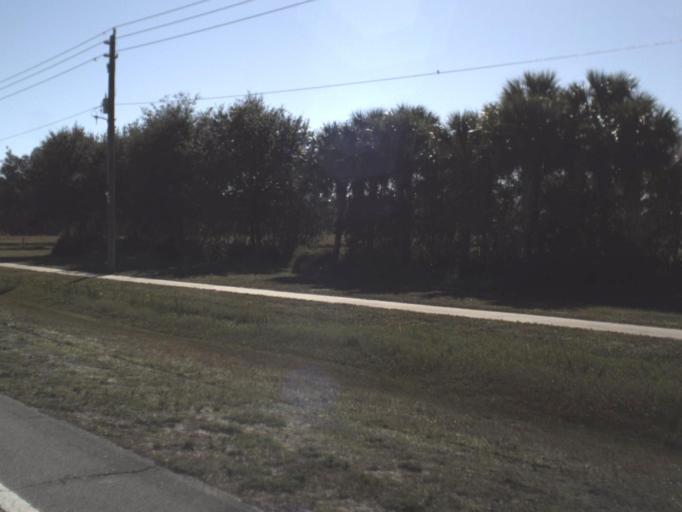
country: US
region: Florida
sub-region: Volusia County
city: Daytona Beach
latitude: 29.1662
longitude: -81.0764
